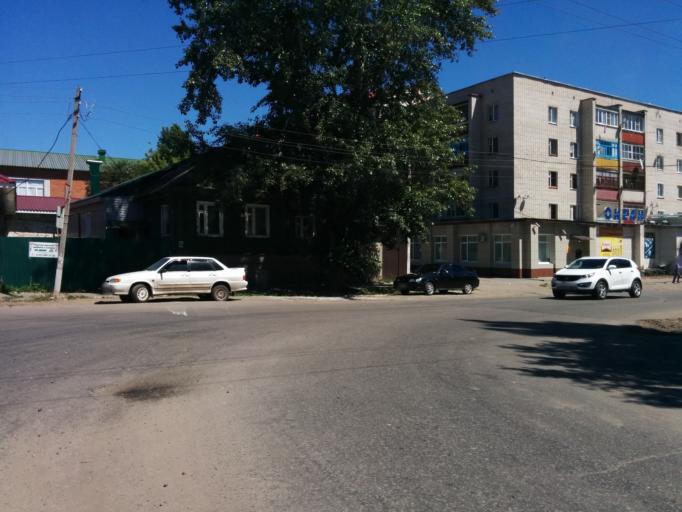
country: RU
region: Tambov
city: Morshansk
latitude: 53.4388
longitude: 41.8020
